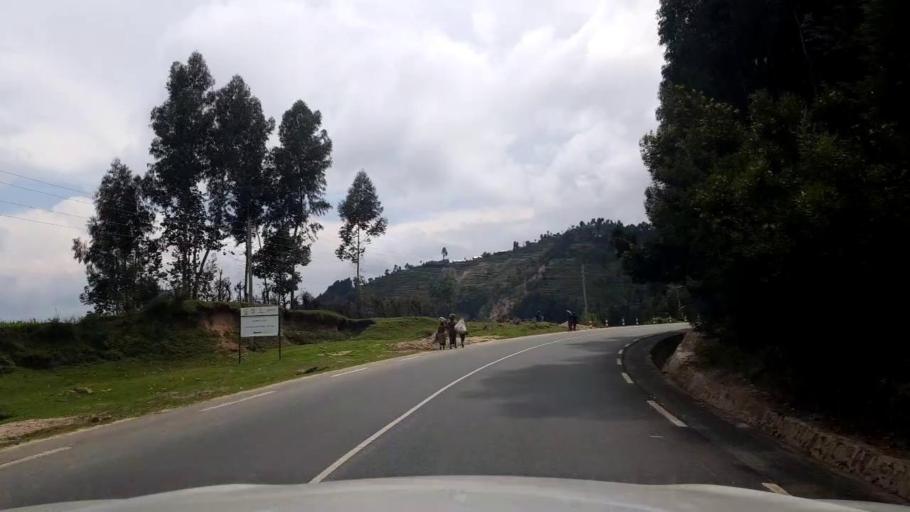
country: RW
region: Northern Province
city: Musanze
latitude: -1.6656
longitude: 29.5177
